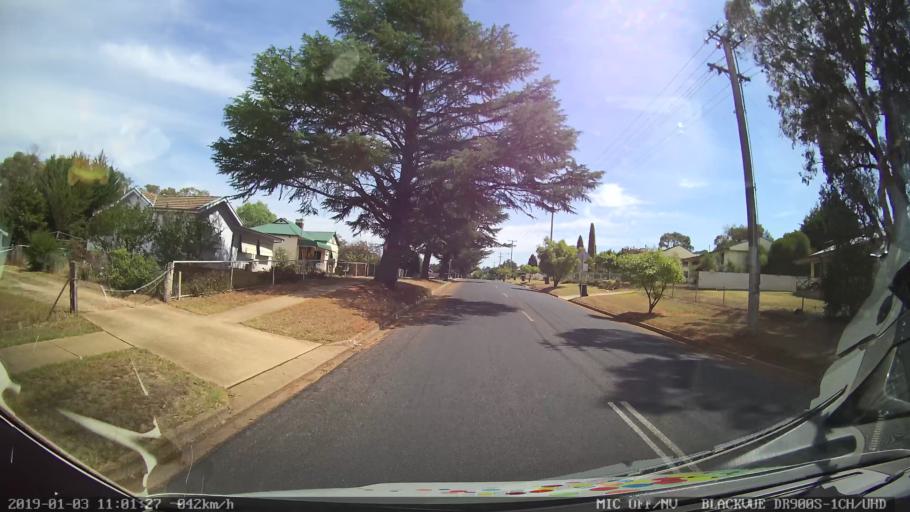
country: AU
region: New South Wales
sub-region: Young
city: Young
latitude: -34.3052
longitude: 148.2994
